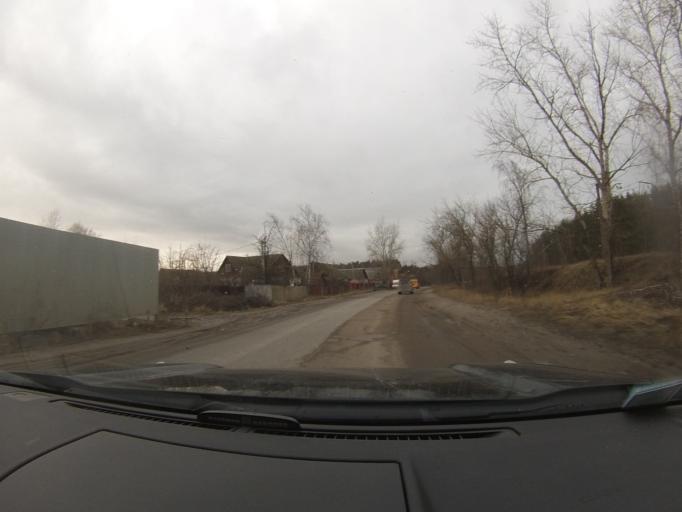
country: RU
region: Moskovskaya
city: Voskresensk
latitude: 55.3303
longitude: 38.6791
